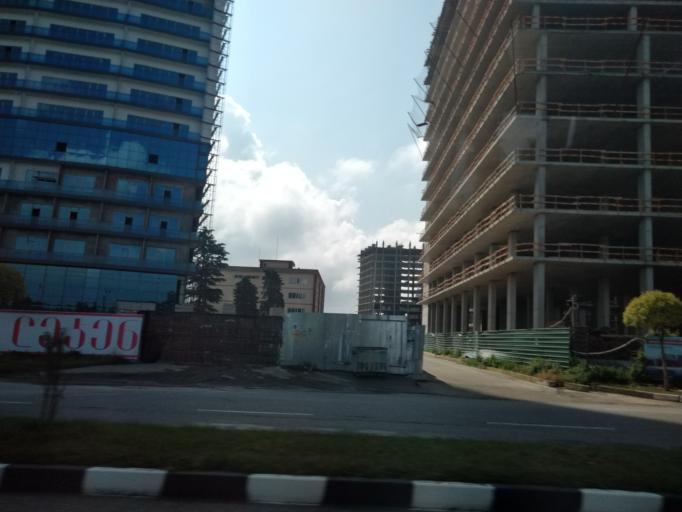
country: GE
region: Ajaria
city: Batumi
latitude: 41.6251
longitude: 41.5976
